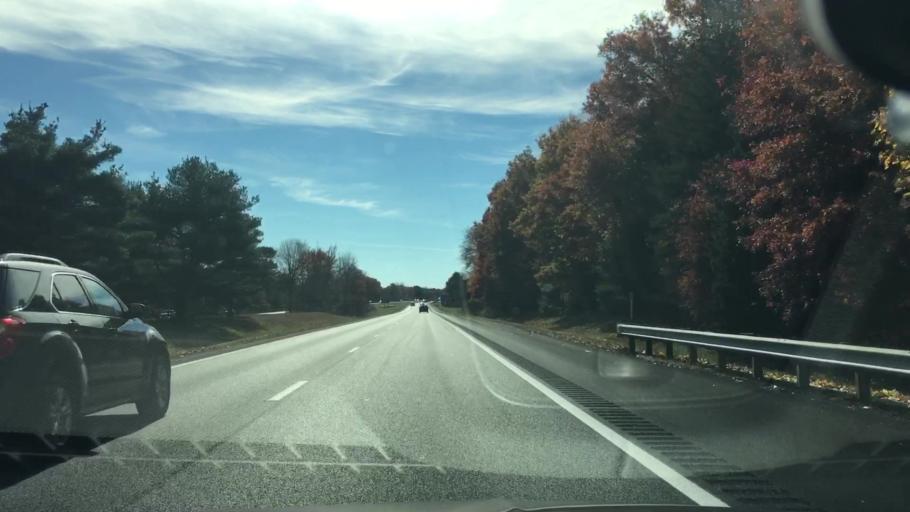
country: US
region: Massachusetts
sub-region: Hampshire County
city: Hatfield
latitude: 42.3759
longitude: -72.6328
